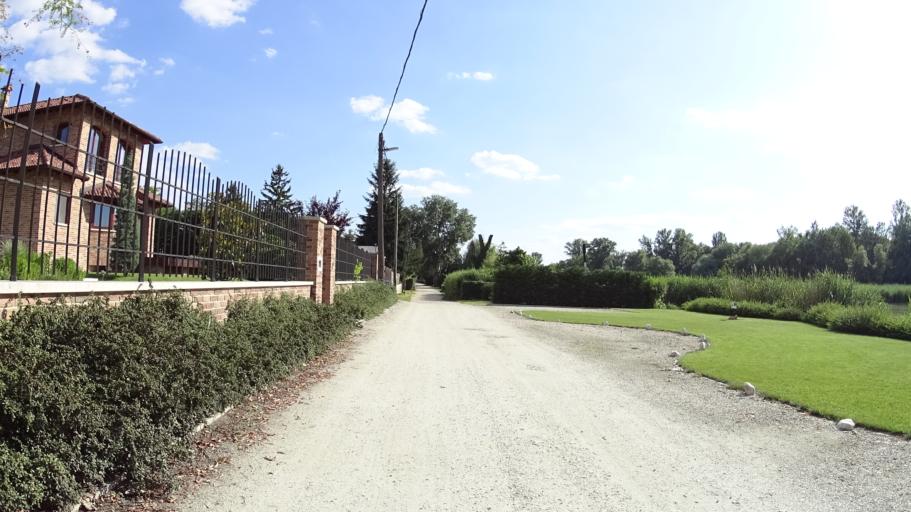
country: HU
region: Pest
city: Dunaharaszti
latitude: 47.3786
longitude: 19.0988
